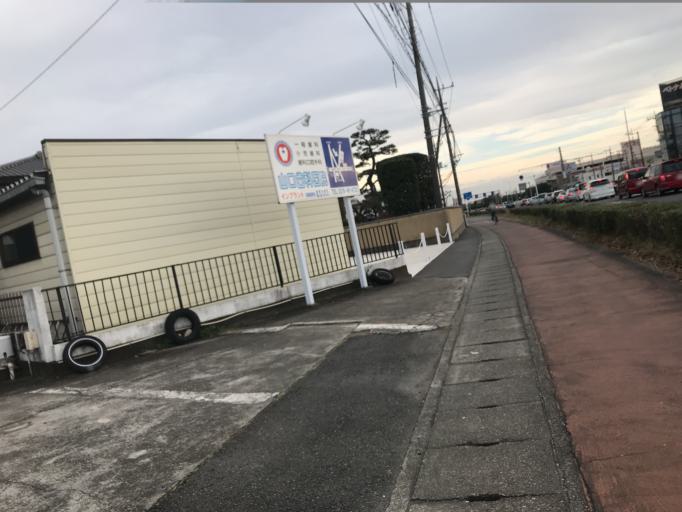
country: JP
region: Gunma
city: Ota
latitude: 36.2994
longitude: 139.3996
